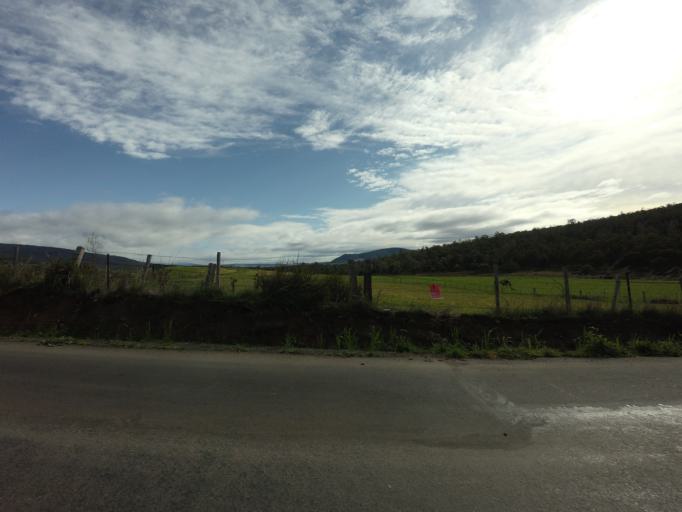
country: AU
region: Tasmania
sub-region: Derwent Valley
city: New Norfolk
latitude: -42.7827
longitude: 146.9990
